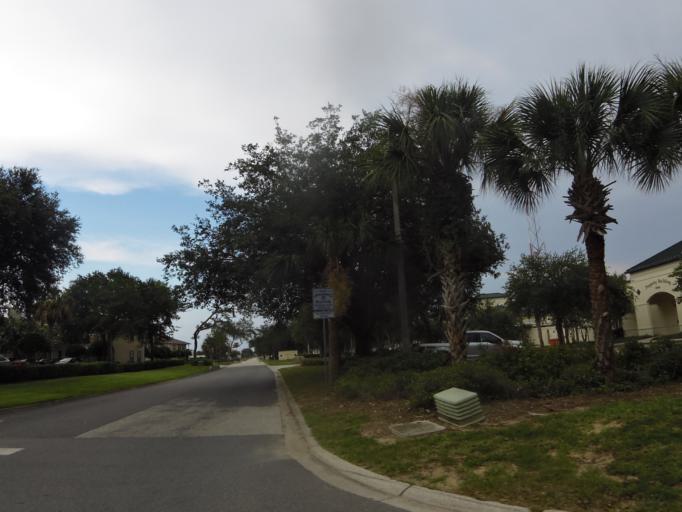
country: US
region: Florida
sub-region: Duval County
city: Jacksonville Beach
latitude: 30.2858
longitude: -81.4070
